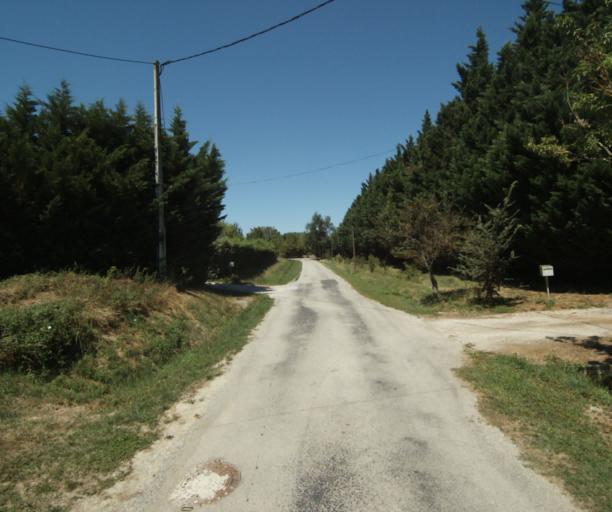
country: FR
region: Midi-Pyrenees
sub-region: Departement de la Haute-Garonne
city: Saint-Felix-Lauragais
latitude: 43.4655
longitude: 1.9316
